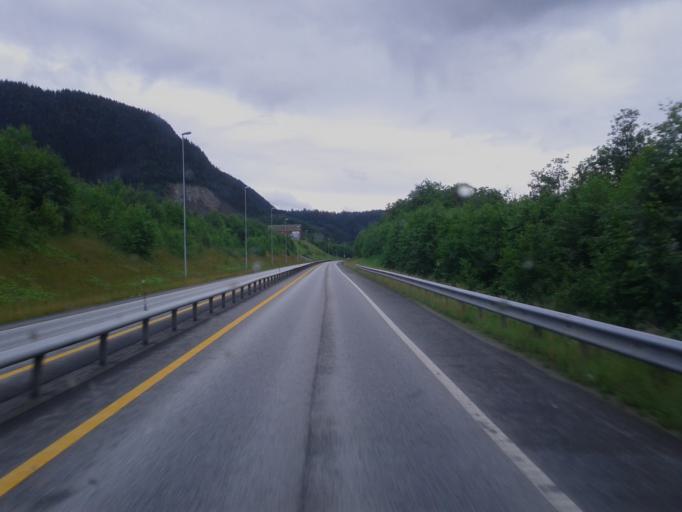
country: NO
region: Sor-Trondelag
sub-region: Melhus
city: Melhus
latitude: 63.2670
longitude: 10.2860
